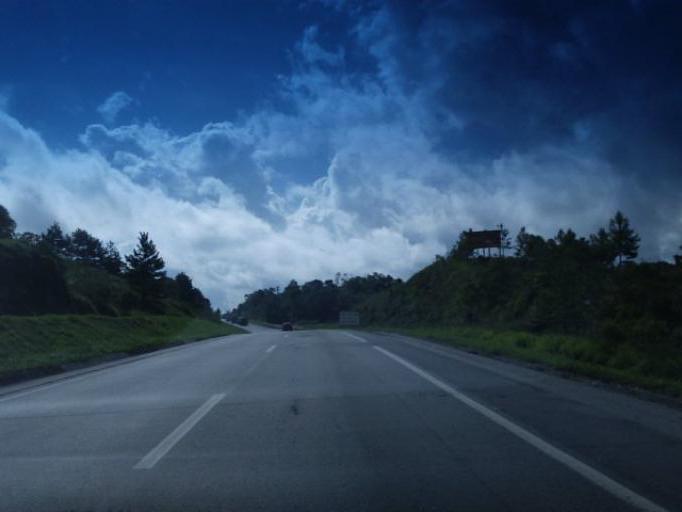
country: BR
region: Parana
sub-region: Antonina
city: Antonina
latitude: -25.1097
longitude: -48.7592
